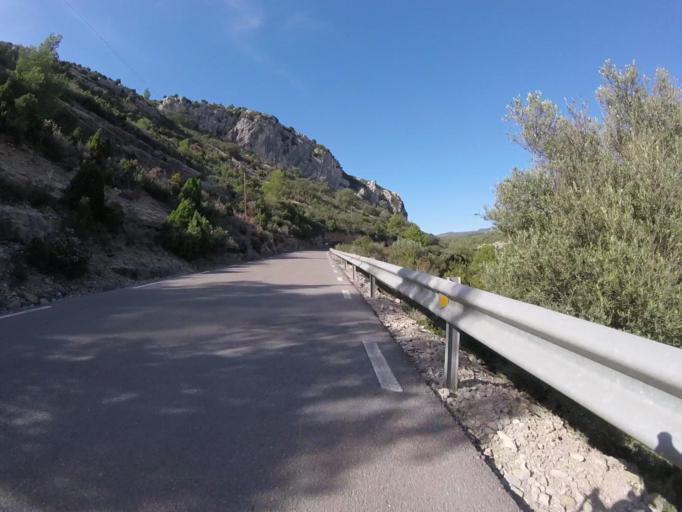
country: ES
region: Valencia
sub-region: Provincia de Castello
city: Sarratella
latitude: 40.2720
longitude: 0.0459
